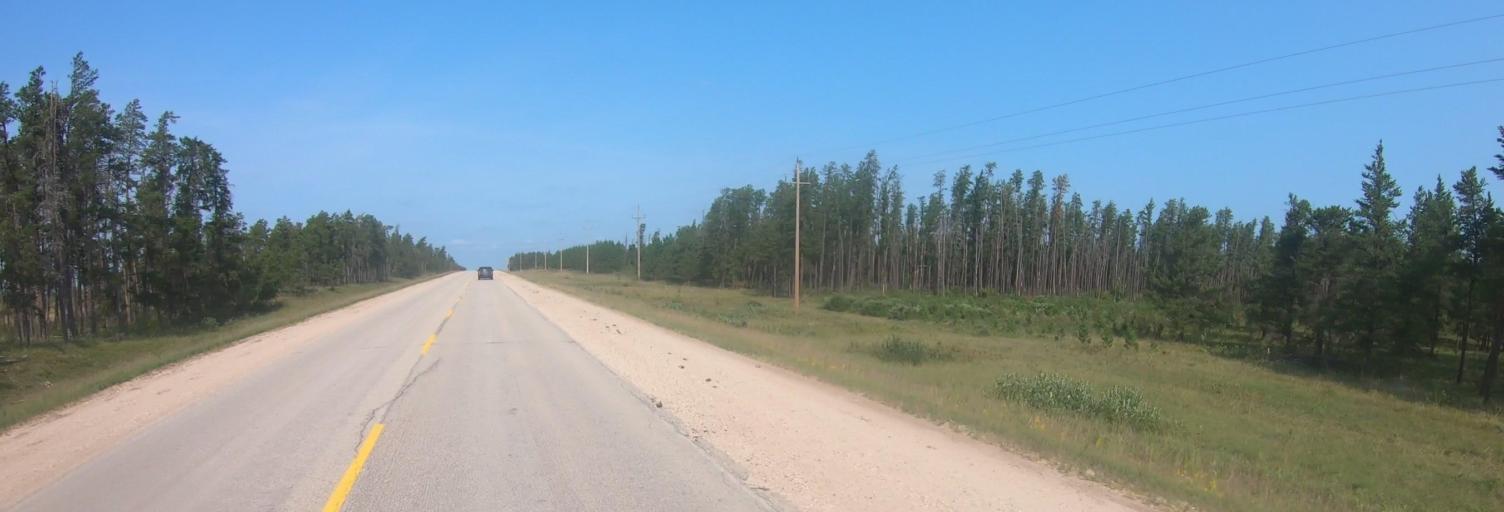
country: US
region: Minnesota
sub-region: Roseau County
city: Roseau
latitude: 49.1303
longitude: -96.0798
